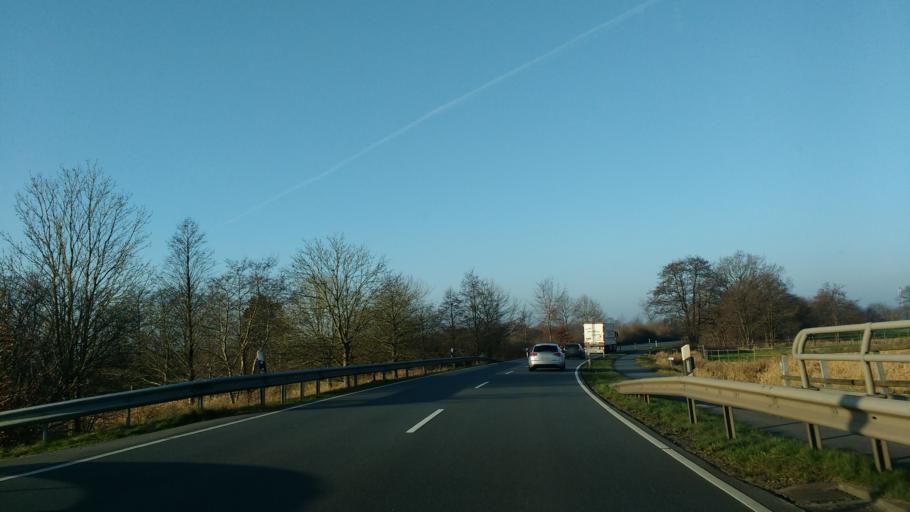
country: DE
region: Schleswig-Holstein
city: Hadenfeld
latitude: 54.0301
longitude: 9.4585
